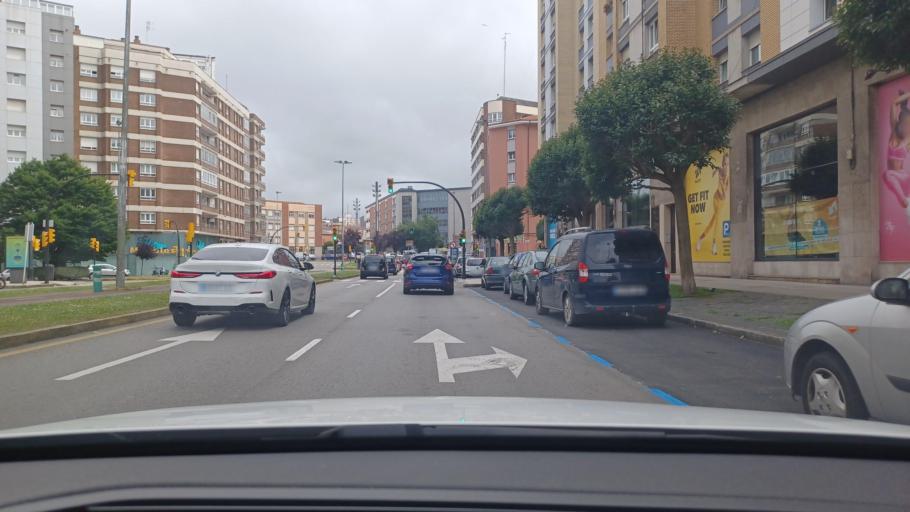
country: ES
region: Asturias
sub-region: Province of Asturias
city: Gijon
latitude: 43.5343
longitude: -5.6713
